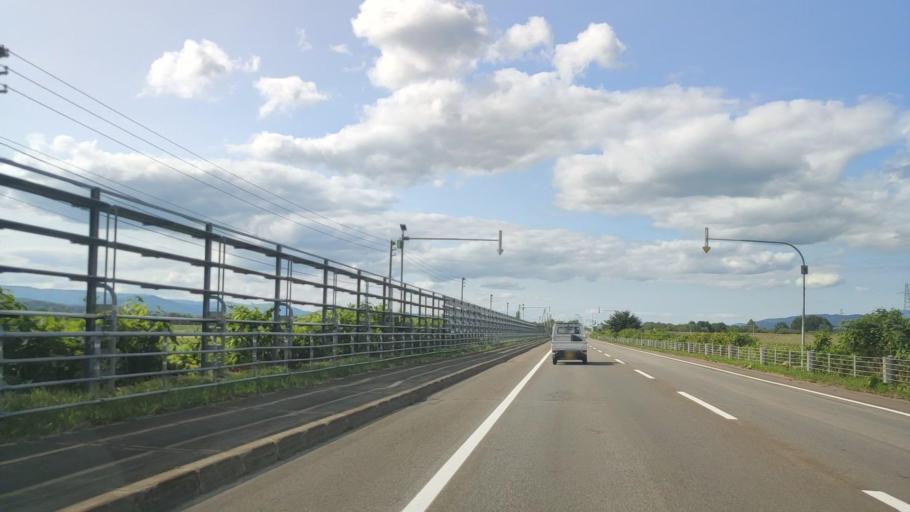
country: JP
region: Hokkaido
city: Nayoro
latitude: 44.4484
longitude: 142.3623
